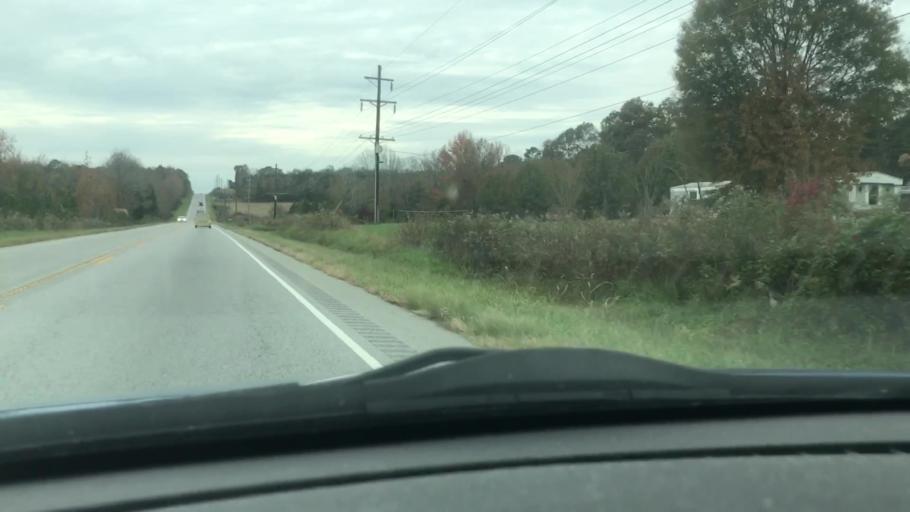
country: US
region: North Carolina
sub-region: Davidson County
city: Thomasville
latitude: 35.7517
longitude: -80.0189
